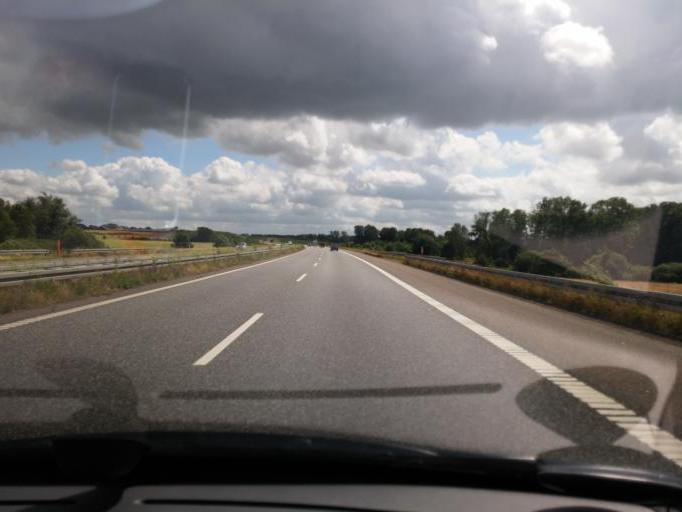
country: DK
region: South Denmark
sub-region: Faaborg-Midtfyn Kommune
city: Arslev
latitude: 55.2930
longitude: 10.4406
